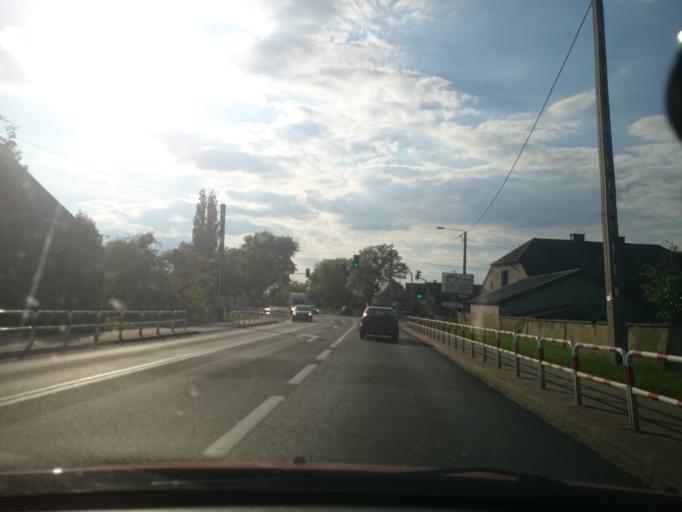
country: PL
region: Opole Voivodeship
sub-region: Powiat strzelecki
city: Izbicko
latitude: 50.5712
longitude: 18.1556
